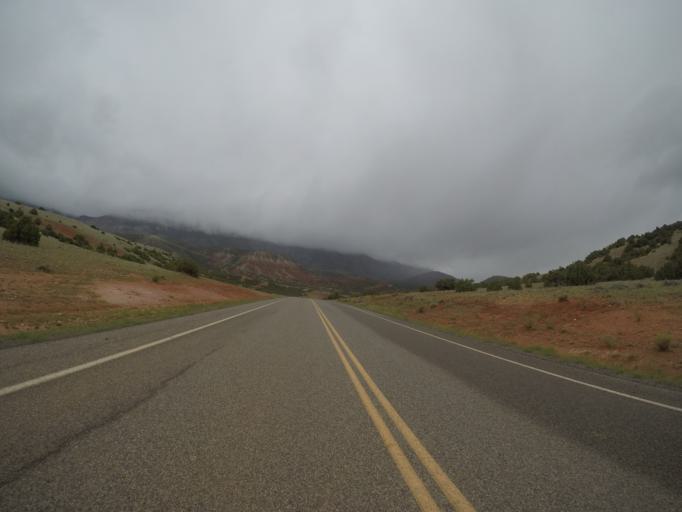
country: US
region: Wyoming
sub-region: Big Horn County
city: Lovell
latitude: 45.1051
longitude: -108.2394
